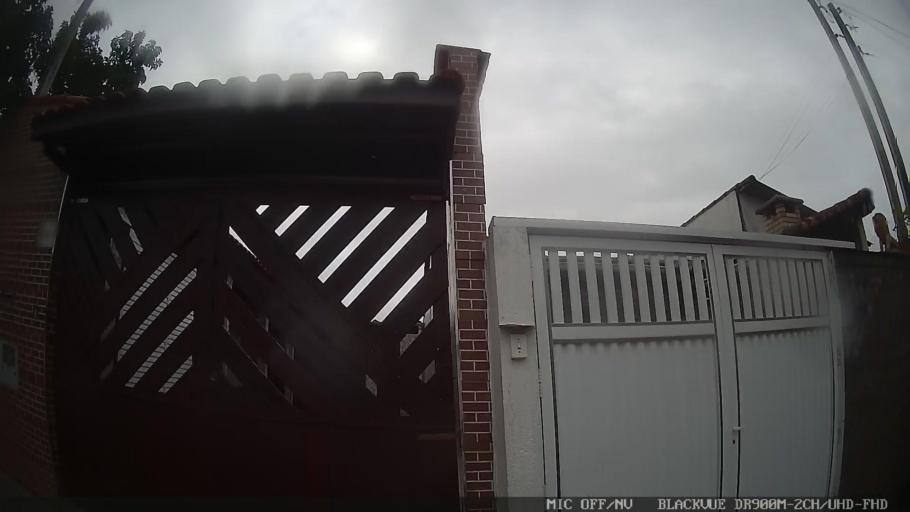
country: BR
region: Sao Paulo
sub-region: Itanhaem
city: Itanhaem
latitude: -24.1866
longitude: -46.8192
